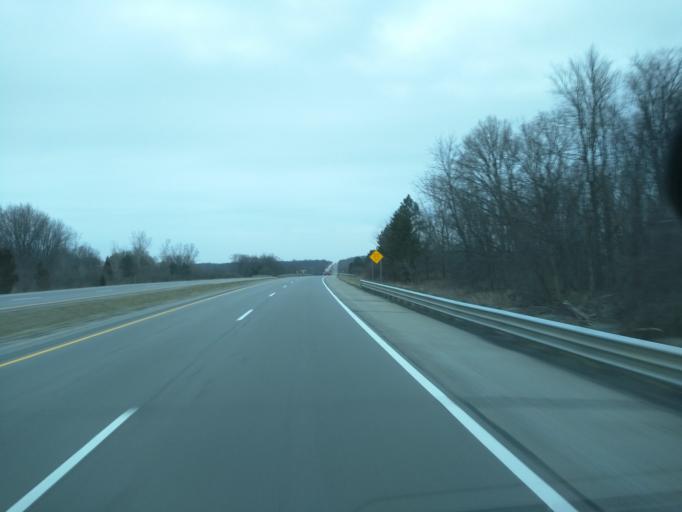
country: US
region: Michigan
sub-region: Ingham County
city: Leslie
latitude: 42.4136
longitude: -84.4294
